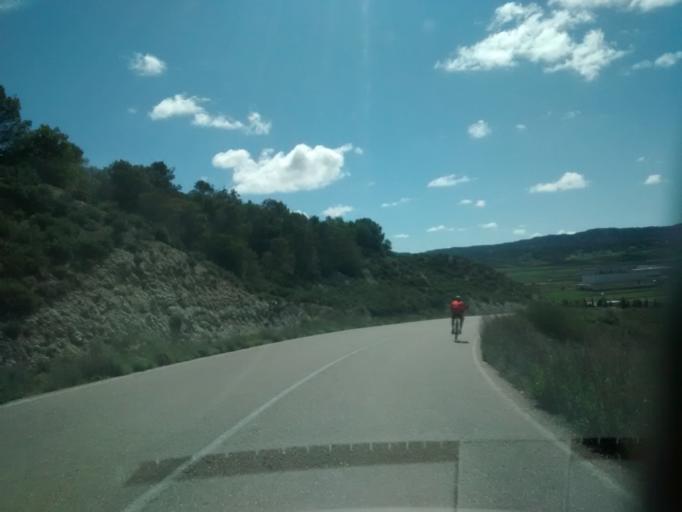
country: ES
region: Aragon
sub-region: Provincia de Zaragoza
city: Lecinena
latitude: 41.7903
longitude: -0.6252
